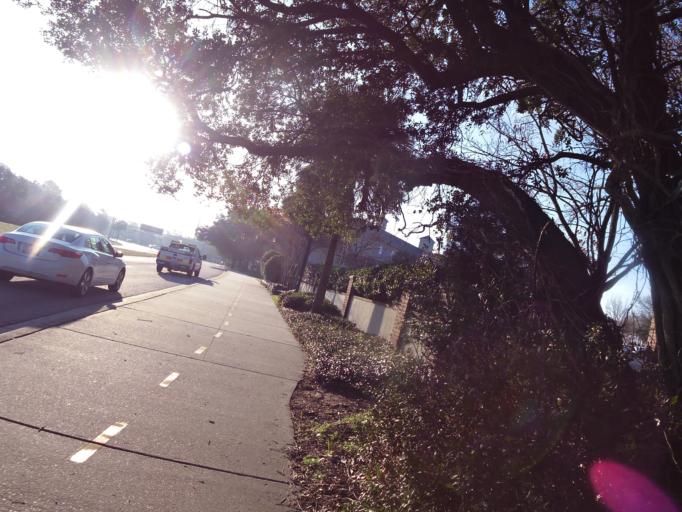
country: US
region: South Carolina
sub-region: Charleston County
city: Mount Pleasant
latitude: 32.7987
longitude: -79.8990
